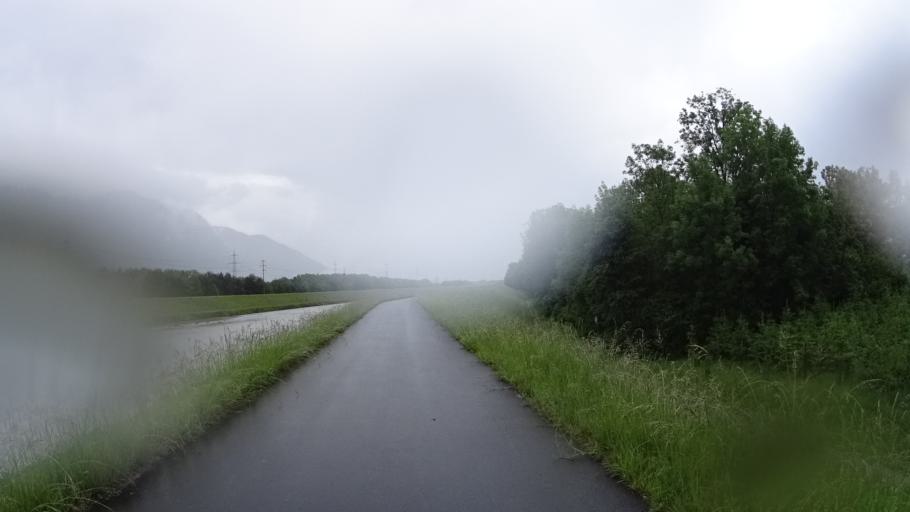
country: LI
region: Gamprin
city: Gamprin
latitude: 47.2236
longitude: 9.5046
